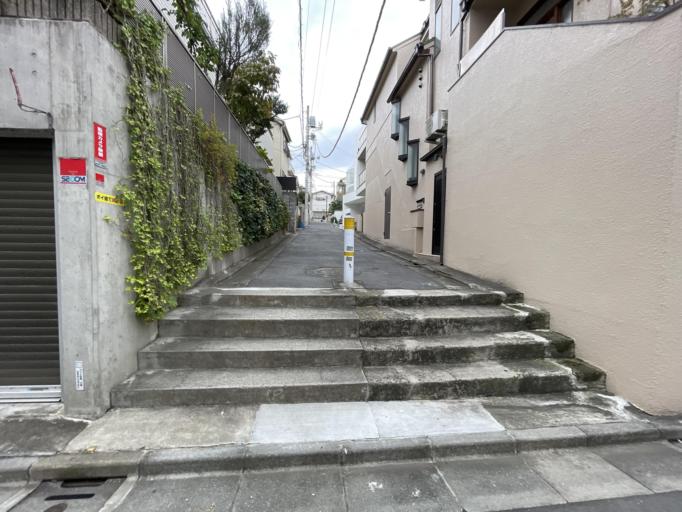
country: JP
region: Tokyo
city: Tokyo
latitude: 35.6176
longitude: 139.6776
